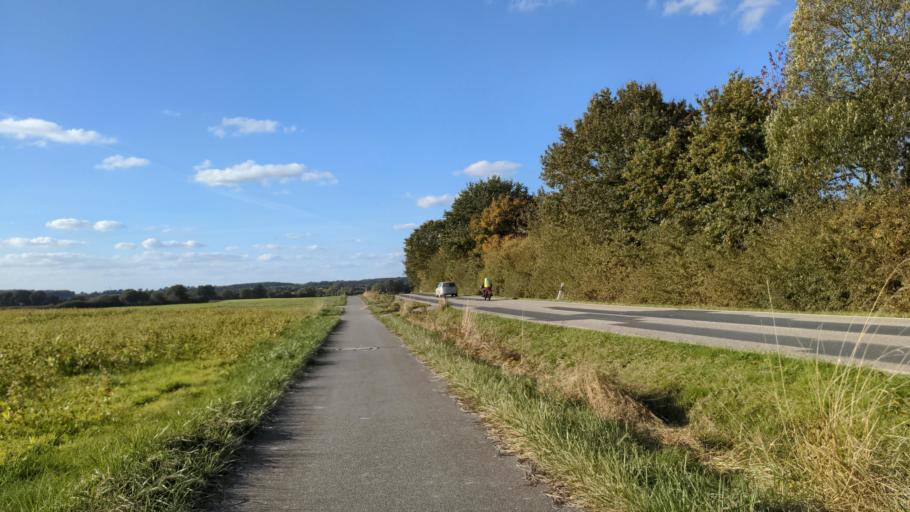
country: DE
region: Schleswig-Holstein
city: Zarpen
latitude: 53.8608
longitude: 10.5369
